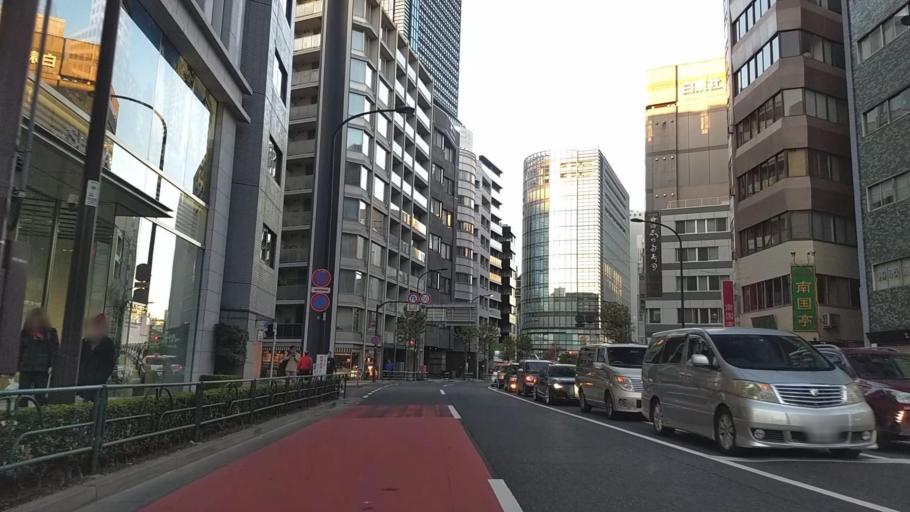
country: JP
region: Tokyo
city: Tokyo
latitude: 35.6956
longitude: 139.7674
